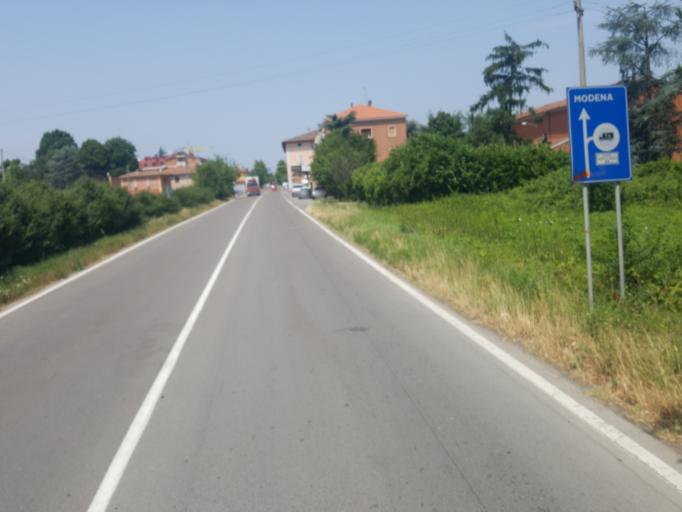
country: IT
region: Emilia-Romagna
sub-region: Provincia di Modena
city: Cavazzona
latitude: 44.5724
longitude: 11.1176
